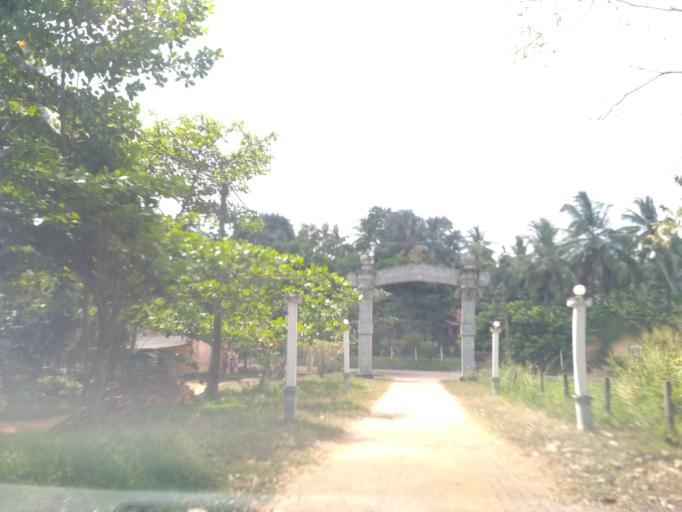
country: LK
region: North Western
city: Kuliyapitiya
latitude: 7.3373
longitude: 80.0621
